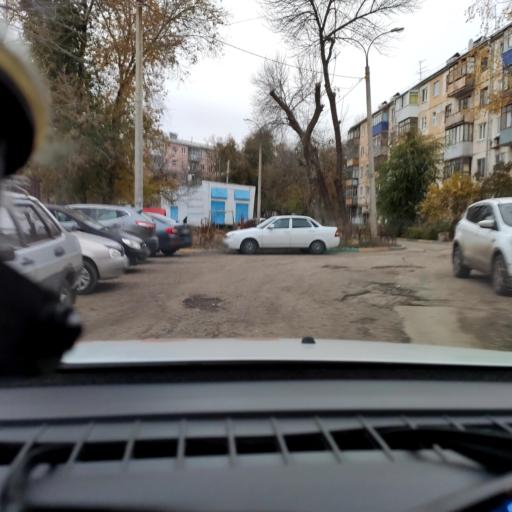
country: RU
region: Samara
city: Samara
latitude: 53.1948
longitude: 50.1661
